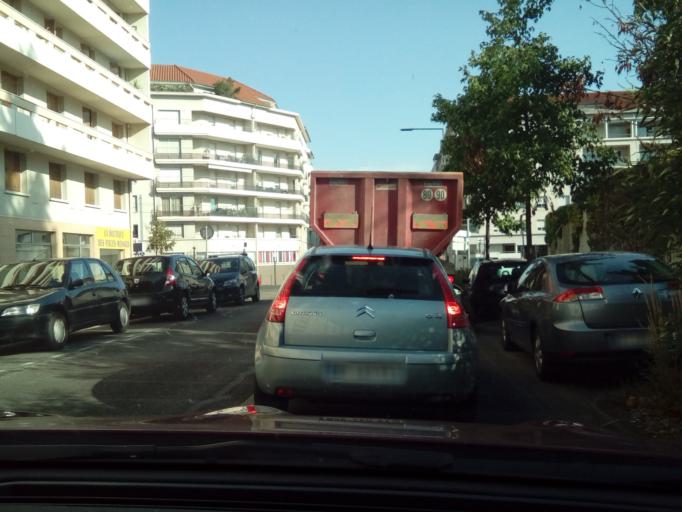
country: FR
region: Rhone-Alpes
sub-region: Departement du Rhone
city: Villeurbanne
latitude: 45.7577
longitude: 4.8853
